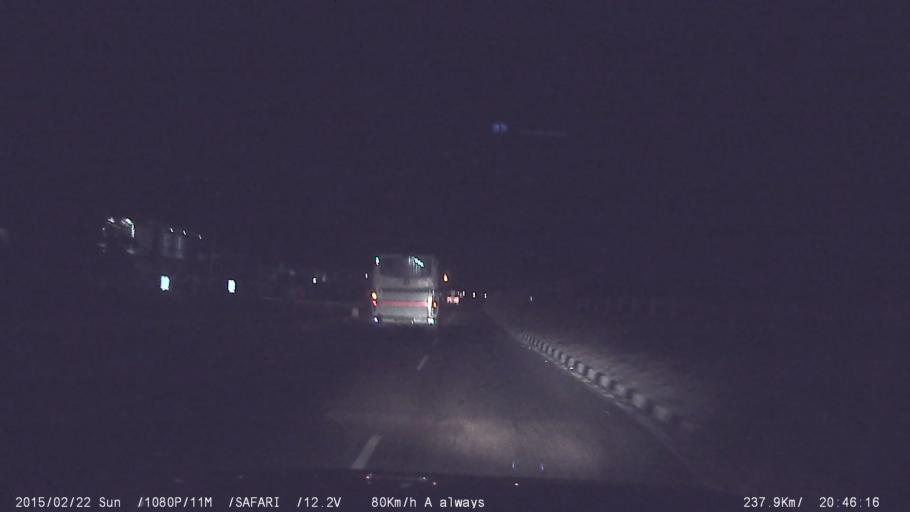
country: IN
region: Tamil Nadu
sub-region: Dindigul
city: Vedasandur
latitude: 10.4804
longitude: 77.9477
